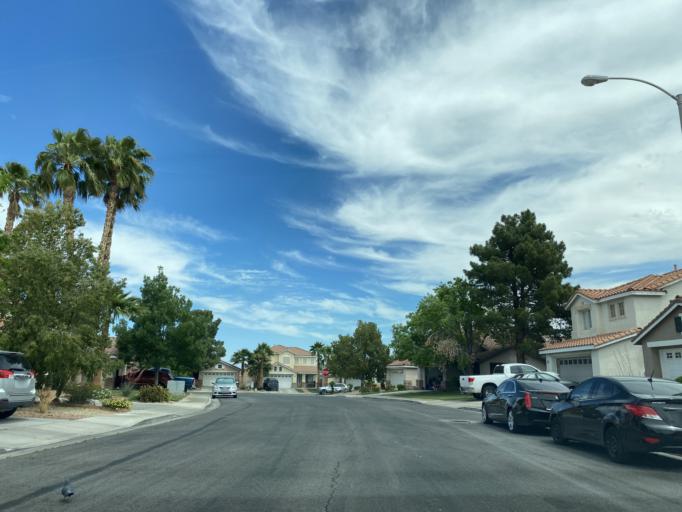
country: US
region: Nevada
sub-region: Clark County
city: Whitney
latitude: 36.0246
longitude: -115.0718
